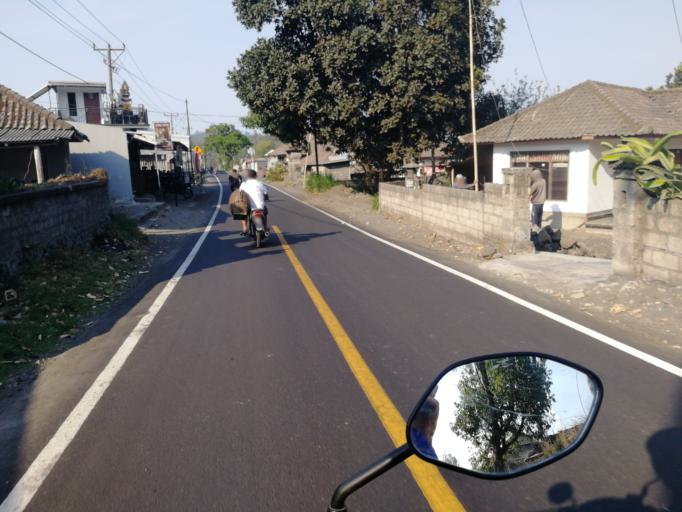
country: ID
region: Bali
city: Banjar Trunyan
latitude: -8.2447
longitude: 115.4006
